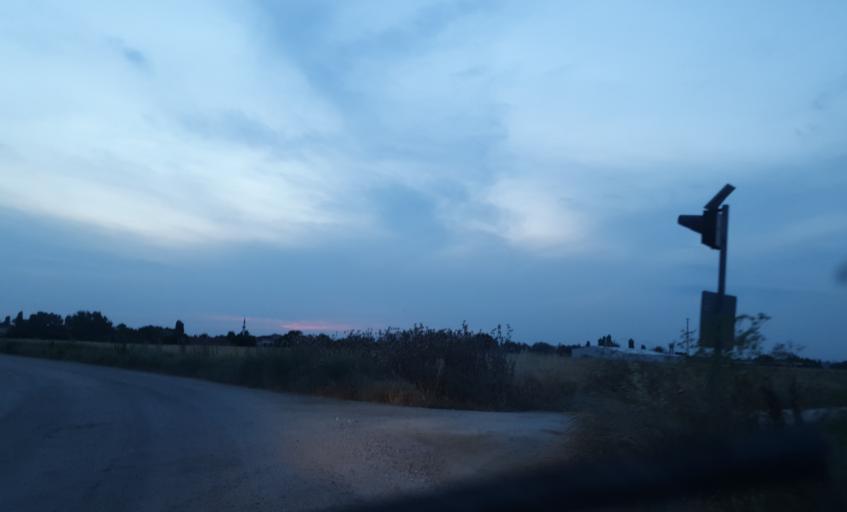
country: TR
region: Kirklareli
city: Vize
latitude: 41.5130
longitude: 27.7456
